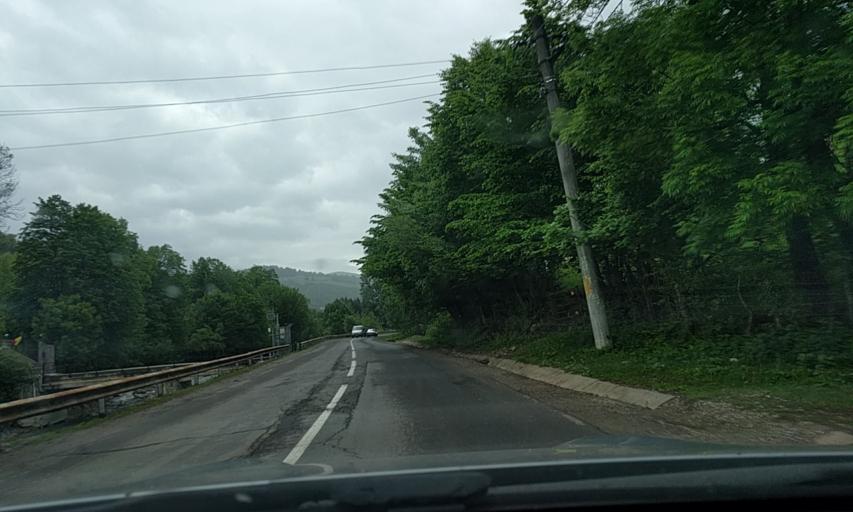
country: RO
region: Dambovita
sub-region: Comuna Moroeni
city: Moroeni
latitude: 45.2303
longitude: 25.4379
